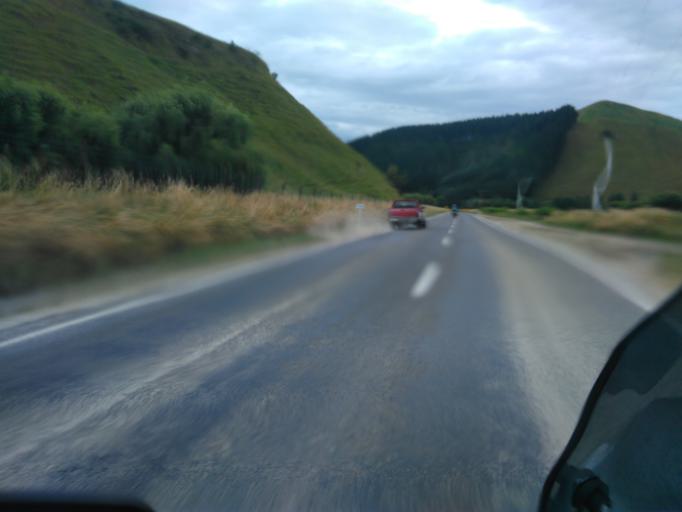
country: NZ
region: Gisborne
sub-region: Gisborne District
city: Gisborne
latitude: -38.4618
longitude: 177.7407
